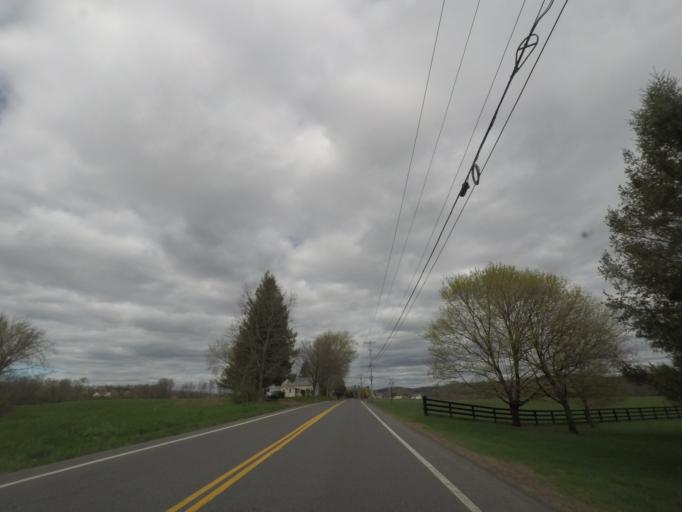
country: US
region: New York
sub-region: Columbia County
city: Philmont
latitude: 42.2839
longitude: -73.6537
